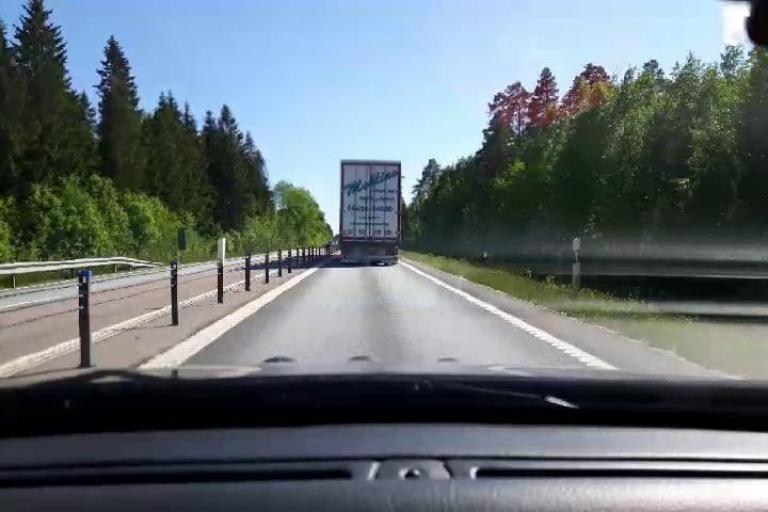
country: SE
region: Gaevleborg
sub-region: Soderhamns Kommun
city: Soderhamn
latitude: 61.2541
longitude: 17.0346
